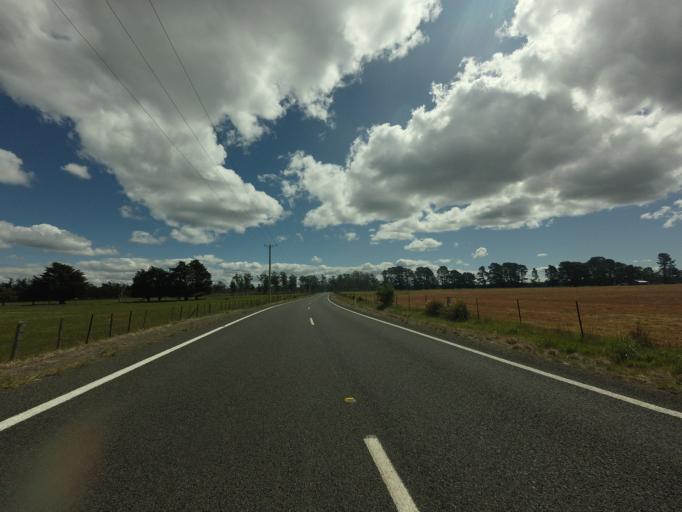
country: AU
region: Tasmania
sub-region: Northern Midlands
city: Evandale
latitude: -41.9898
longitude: 147.6983
